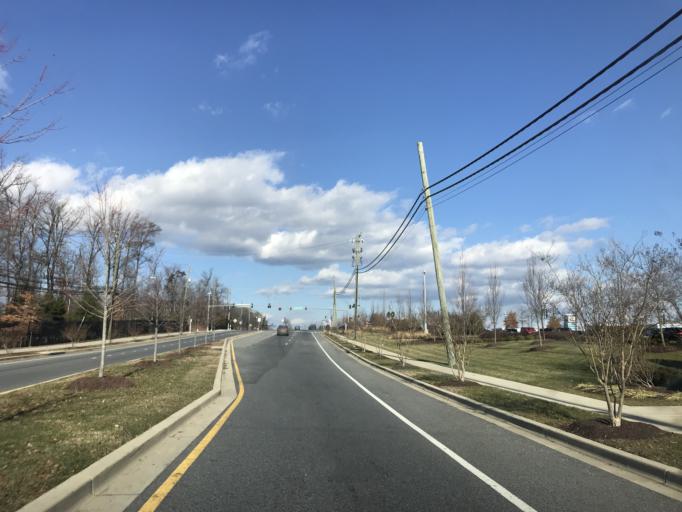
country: US
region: Maryland
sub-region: Prince George's County
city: Forest Heights
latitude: 38.7928
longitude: -77.0039
